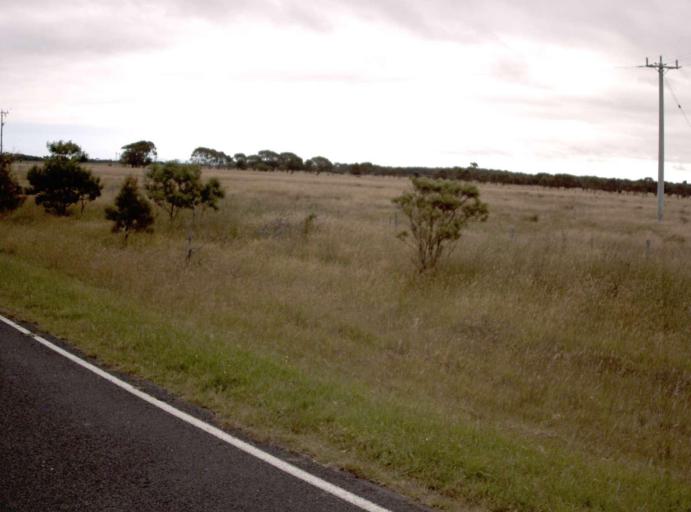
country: AU
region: Victoria
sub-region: Wellington
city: Sale
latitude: -38.5731
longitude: 146.8777
